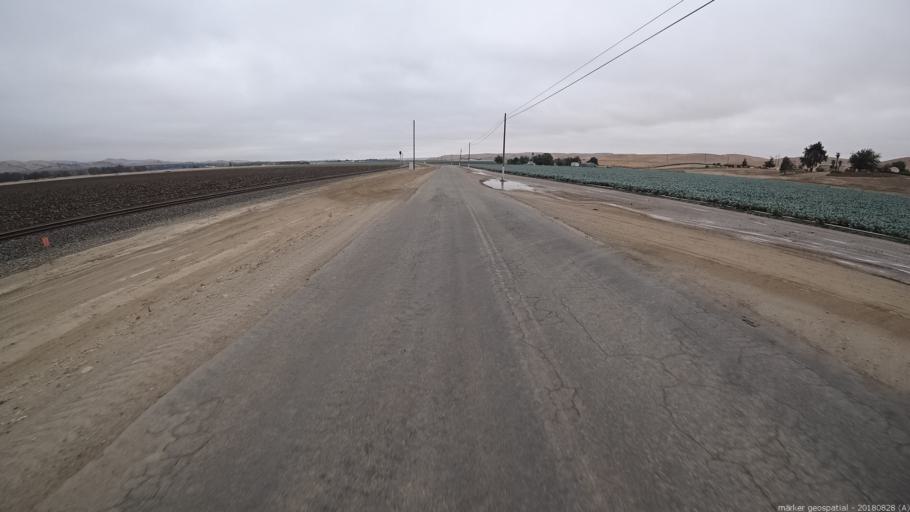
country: US
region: California
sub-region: San Luis Obispo County
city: Lake Nacimiento
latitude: 35.9905
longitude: -120.8811
